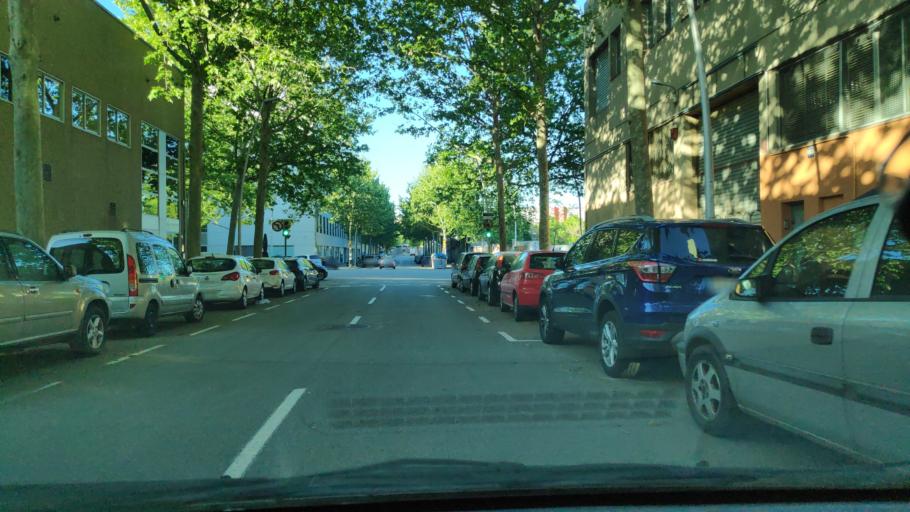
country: ES
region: Catalonia
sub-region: Provincia de Barcelona
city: Sant Marti
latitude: 41.4114
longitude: 2.2092
